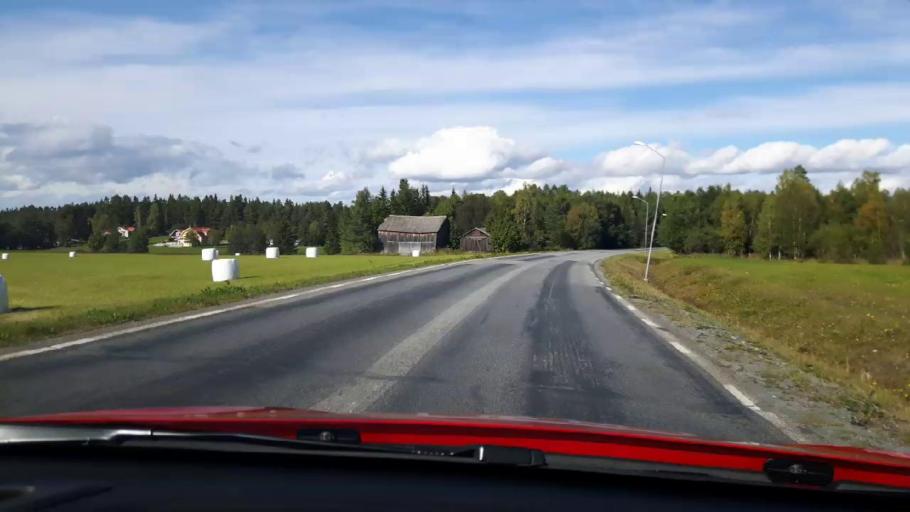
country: SE
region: Jaemtland
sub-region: Krokoms Kommun
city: Krokom
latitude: 63.1183
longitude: 14.4318
